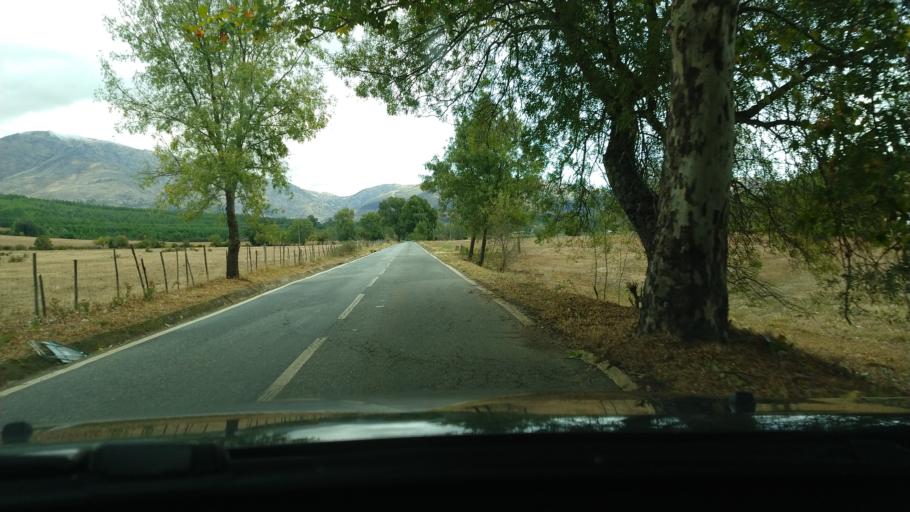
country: PT
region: Castelo Branco
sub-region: Covilha
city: Covilha
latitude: 40.2305
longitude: -7.6055
